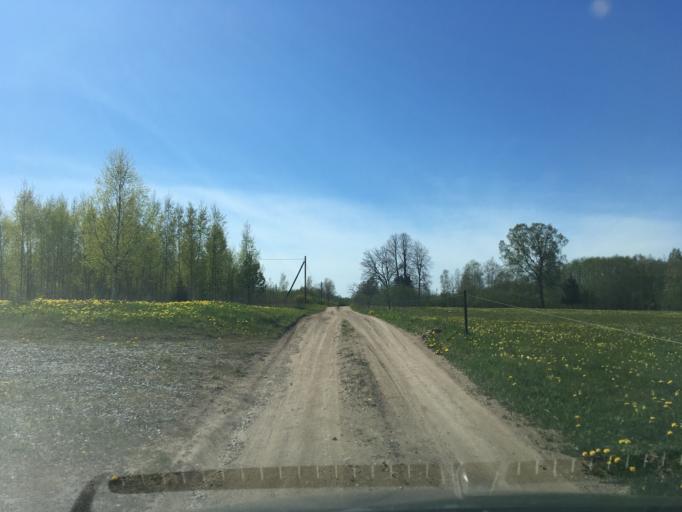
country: EE
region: Harju
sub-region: Raasiku vald
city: Arukula
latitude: 59.2642
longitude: 25.1086
